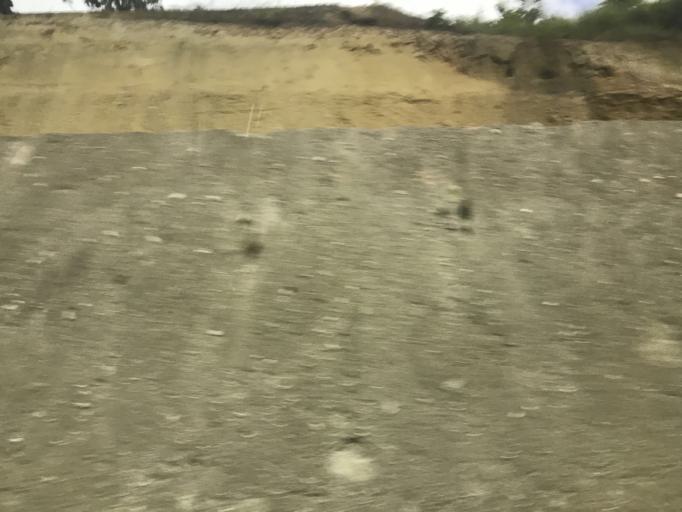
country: GT
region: Chimaltenango
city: El Tejar
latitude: 14.6374
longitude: -90.7887
